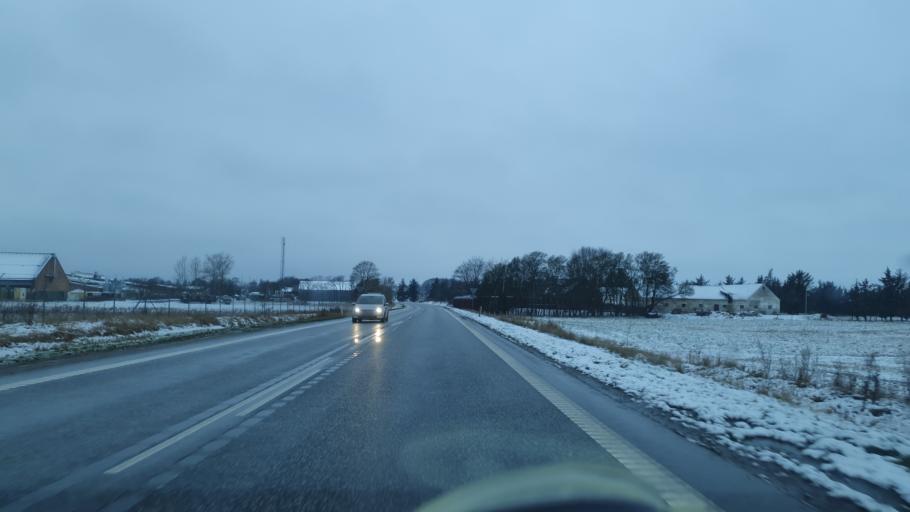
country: DK
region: North Denmark
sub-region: Alborg Kommune
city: Vestbjerg
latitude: 57.0889
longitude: 9.9546
